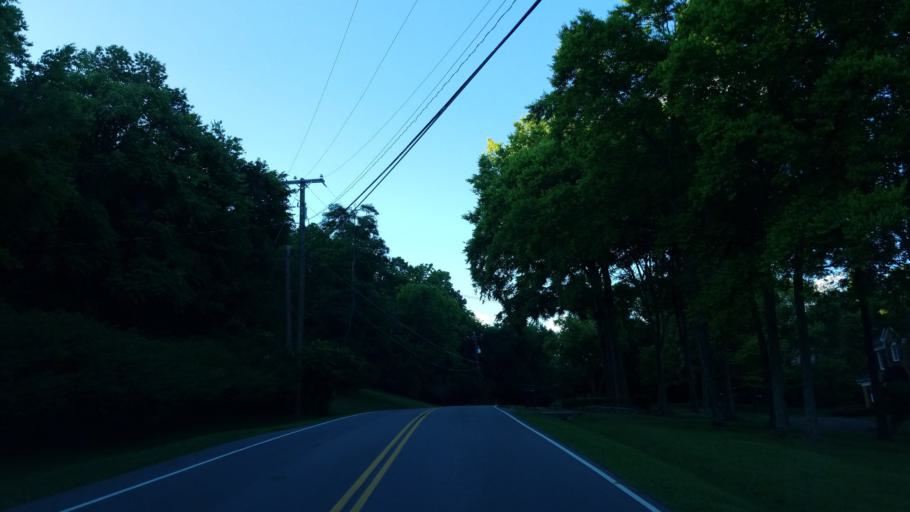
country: US
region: Tennessee
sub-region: Williamson County
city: Brentwood
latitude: 36.0462
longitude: -86.7830
